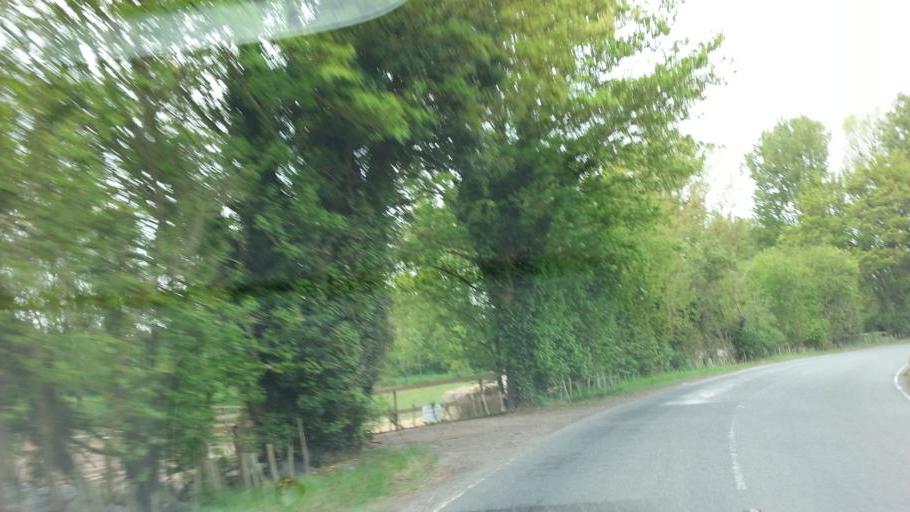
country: GB
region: England
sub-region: Suffolk
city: Lavenham
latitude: 52.0893
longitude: 0.8531
